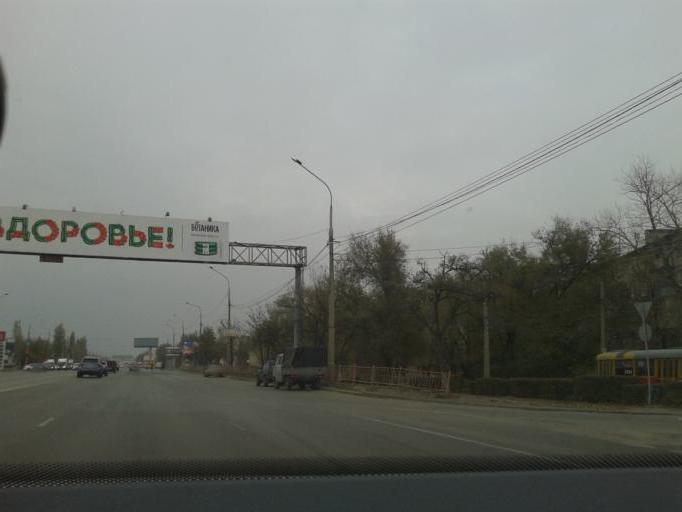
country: RU
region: Volgograd
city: Volgograd
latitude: 48.7566
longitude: 44.4805
